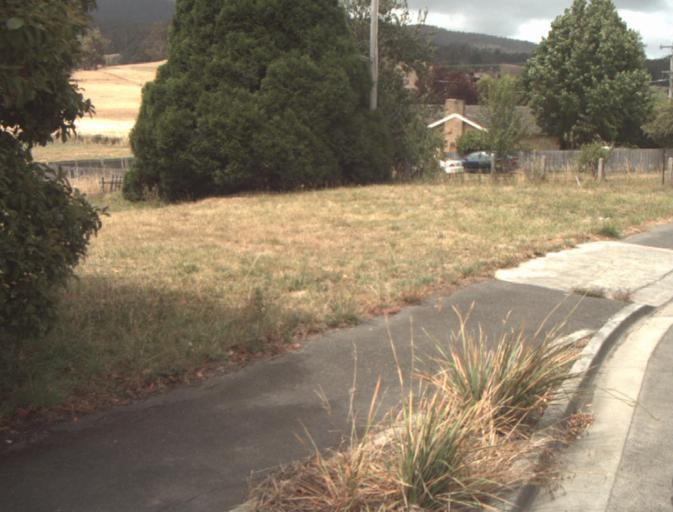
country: AU
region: Tasmania
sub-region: Launceston
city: Mayfield
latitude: -41.2539
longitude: 147.2157
